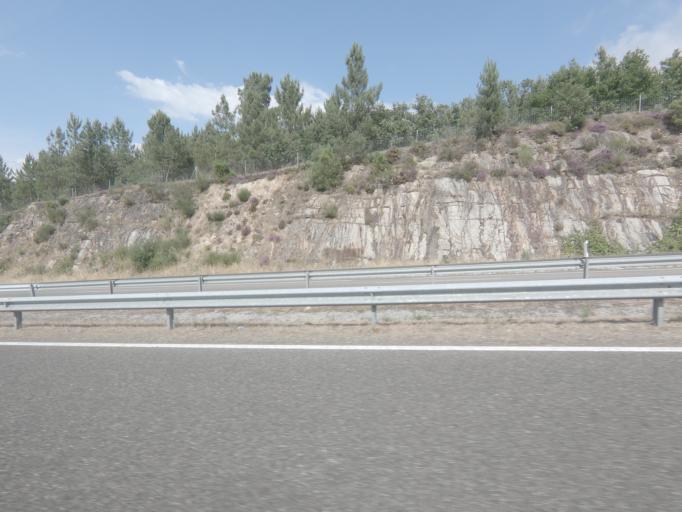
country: ES
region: Galicia
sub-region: Provincia de Ourense
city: Taboadela
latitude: 42.2703
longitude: -7.8716
